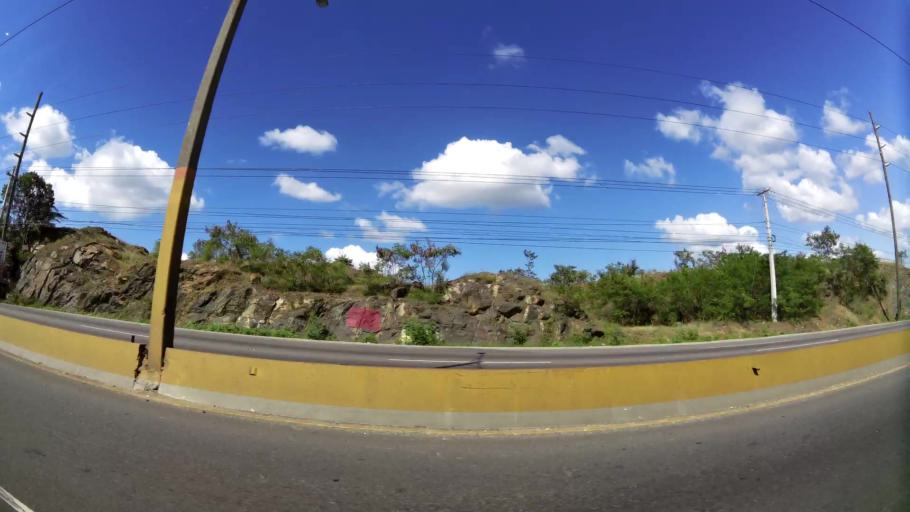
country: DO
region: Santo Domingo
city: Santo Domingo Oeste
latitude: 18.5477
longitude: -70.0422
